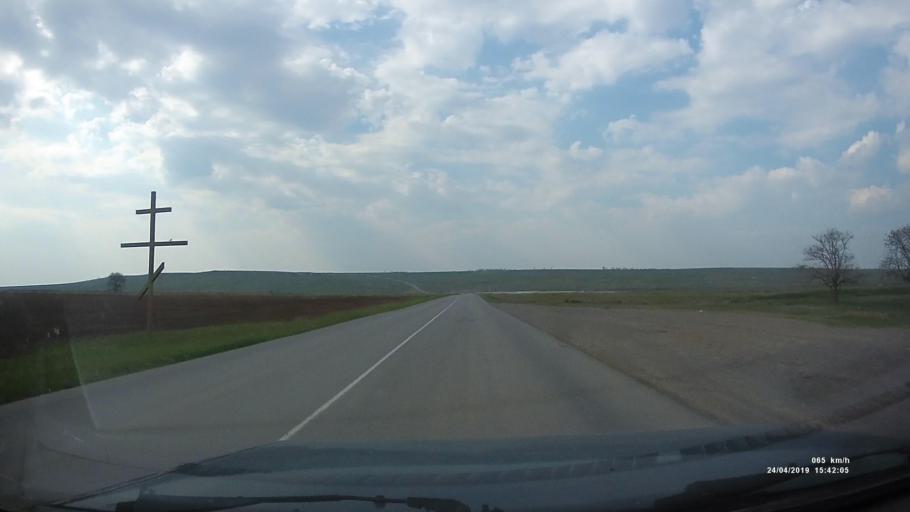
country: RU
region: Kalmykiya
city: Yashalta
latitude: 46.5730
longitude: 42.7918
